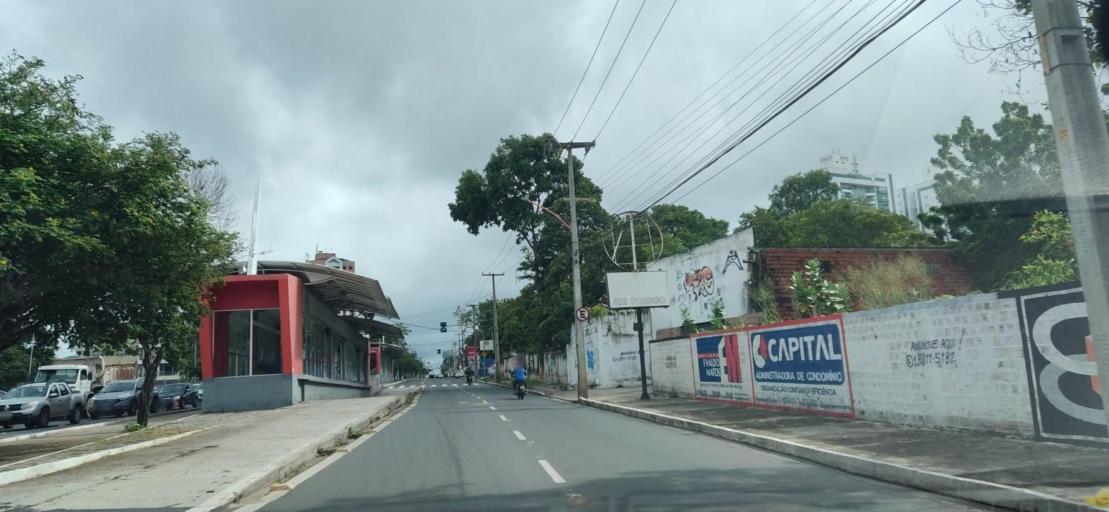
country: BR
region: Piaui
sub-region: Teresina
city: Teresina
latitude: -5.0688
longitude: -42.7711
